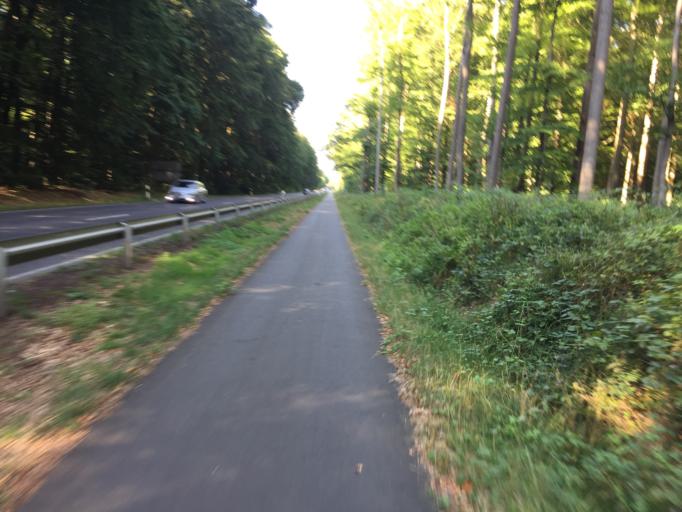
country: DE
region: Hesse
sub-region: Regierungsbezirk Giessen
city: Langgons
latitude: 50.5424
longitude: 8.6748
